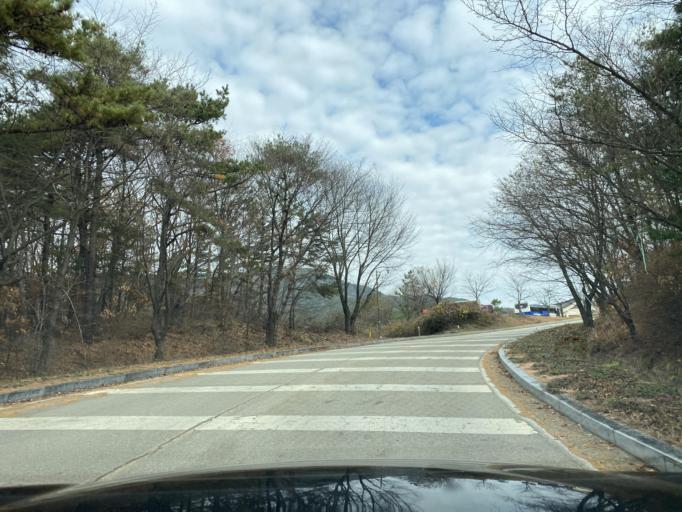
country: KR
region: Chungcheongnam-do
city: Hongsung
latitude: 36.6549
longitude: 126.6198
